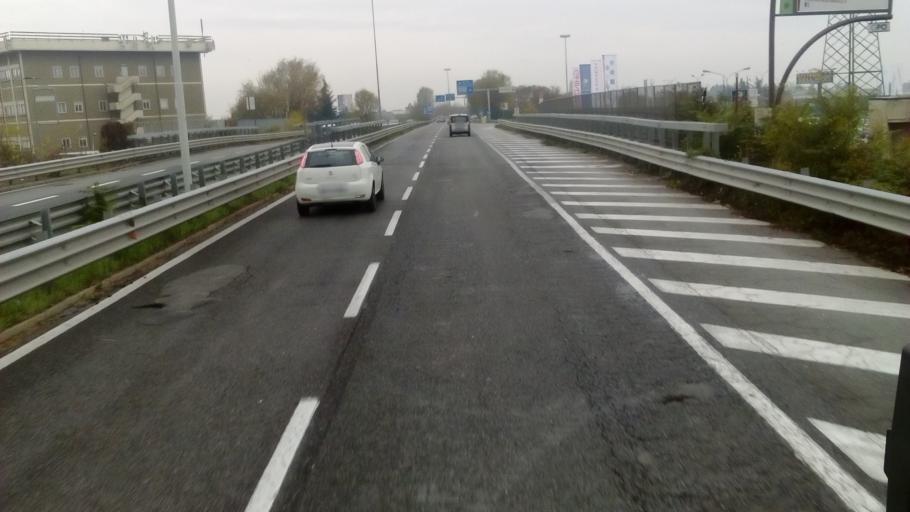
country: IT
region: Lombardy
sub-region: Provincia di Bergamo
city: Bergamo
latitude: 45.6791
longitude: 9.6732
